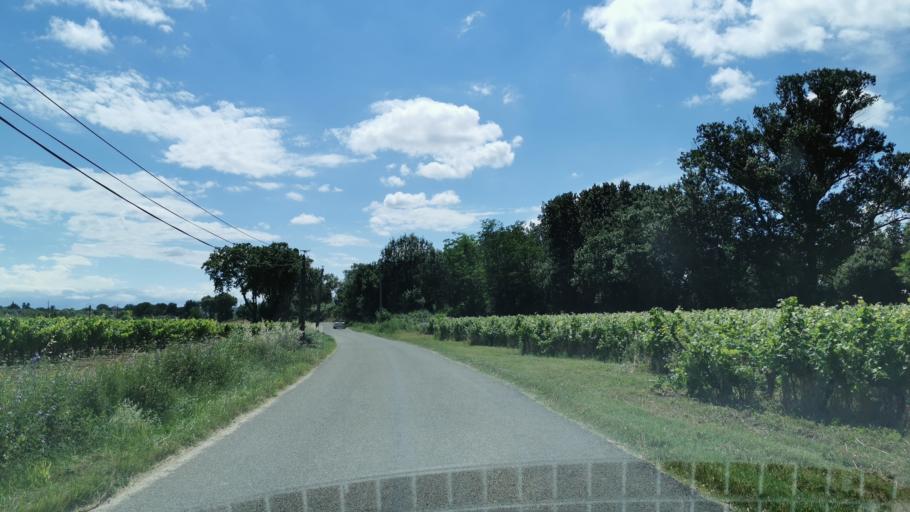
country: FR
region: Languedoc-Roussillon
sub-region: Departement de l'Aude
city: Marcorignan
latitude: 43.2346
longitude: 2.9287
